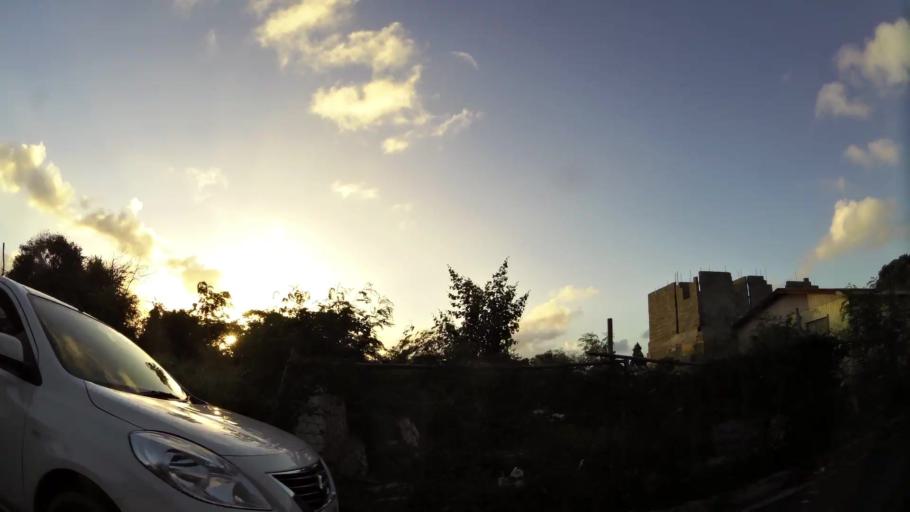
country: AG
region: Saint John
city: Saint John's
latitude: 17.1309
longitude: -61.8383
